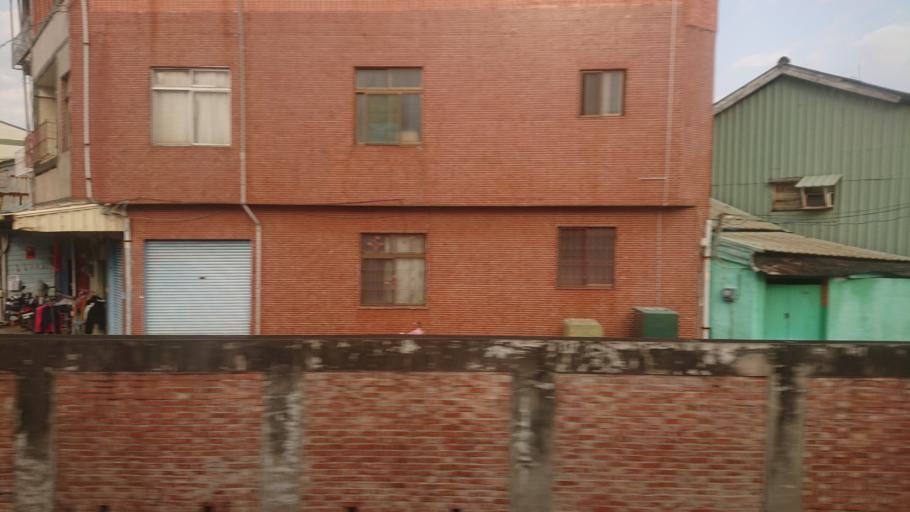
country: TW
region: Taiwan
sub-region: Chiayi
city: Jiayi Shi
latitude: 23.4847
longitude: 120.4458
